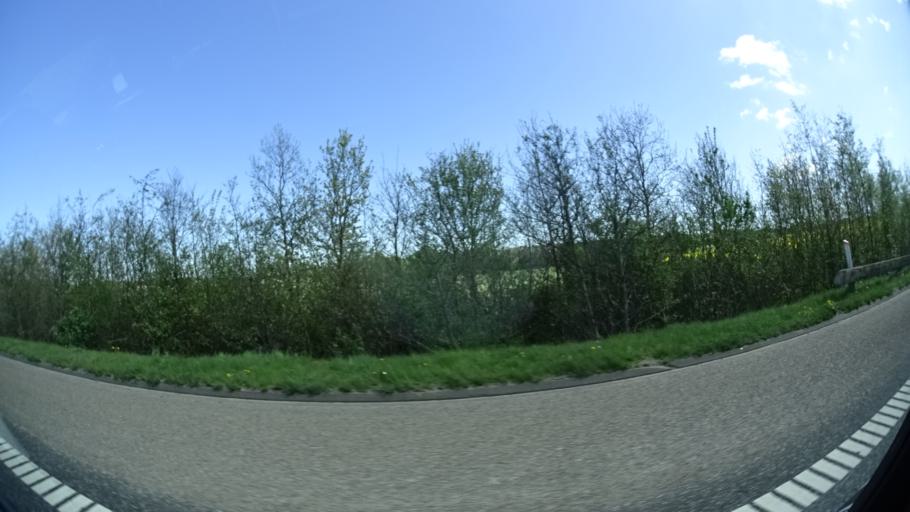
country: DK
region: Central Jutland
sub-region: Arhus Kommune
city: Framlev
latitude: 56.1315
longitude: 10.0348
